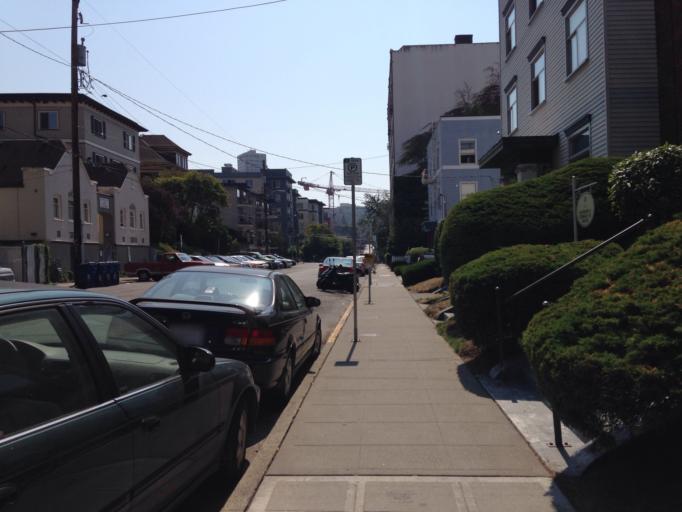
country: US
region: Washington
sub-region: King County
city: Seattle
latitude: 47.6174
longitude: -122.3246
